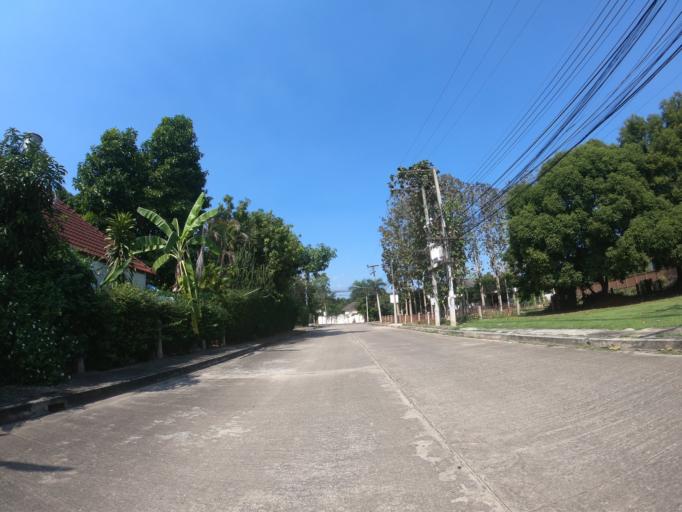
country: TH
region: Chiang Mai
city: Saraphi
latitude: 18.7502
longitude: 99.0140
